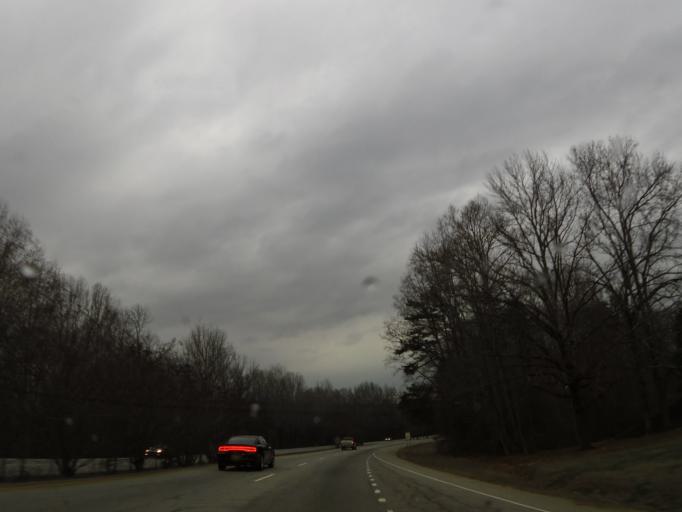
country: US
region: South Carolina
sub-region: Greenville County
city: Sans Souci
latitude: 34.9166
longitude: -82.4315
